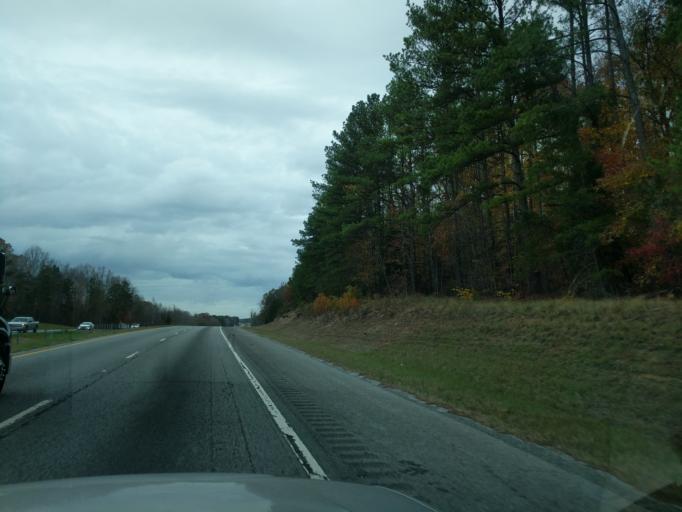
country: US
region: South Carolina
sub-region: Laurens County
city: Watts Mills
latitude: 34.6222
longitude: -81.9042
